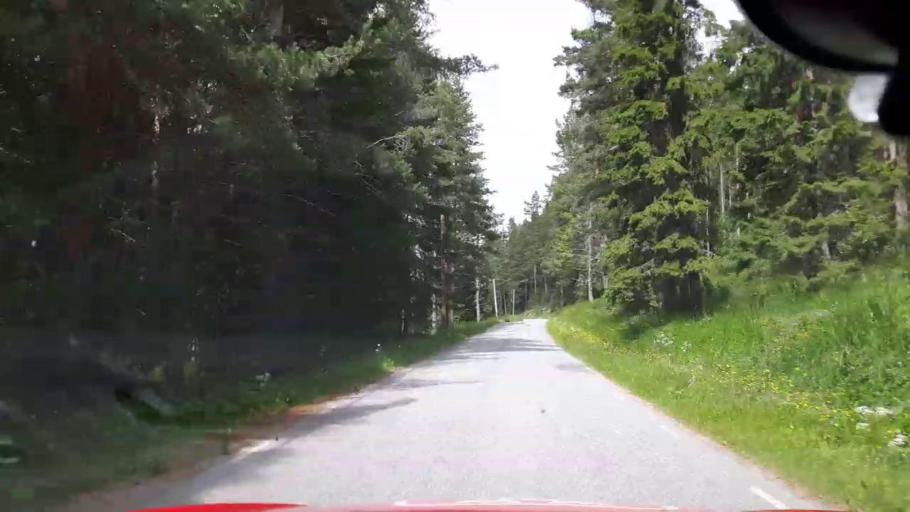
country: SE
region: Jaemtland
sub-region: Braecke Kommun
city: Braecke
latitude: 62.8587
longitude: 15.2801
